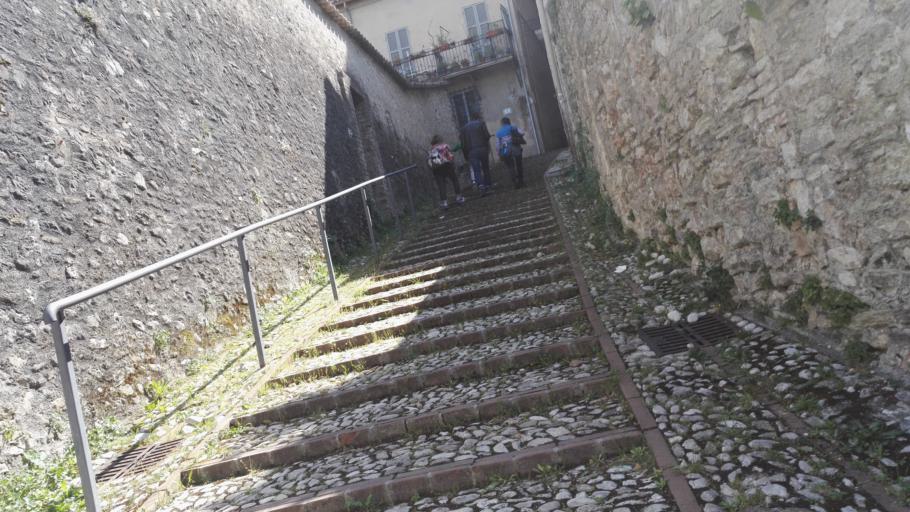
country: IT
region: Umbria
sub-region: Provincia di Perugia
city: Spoleto
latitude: 42.7368
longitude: 12.7368
